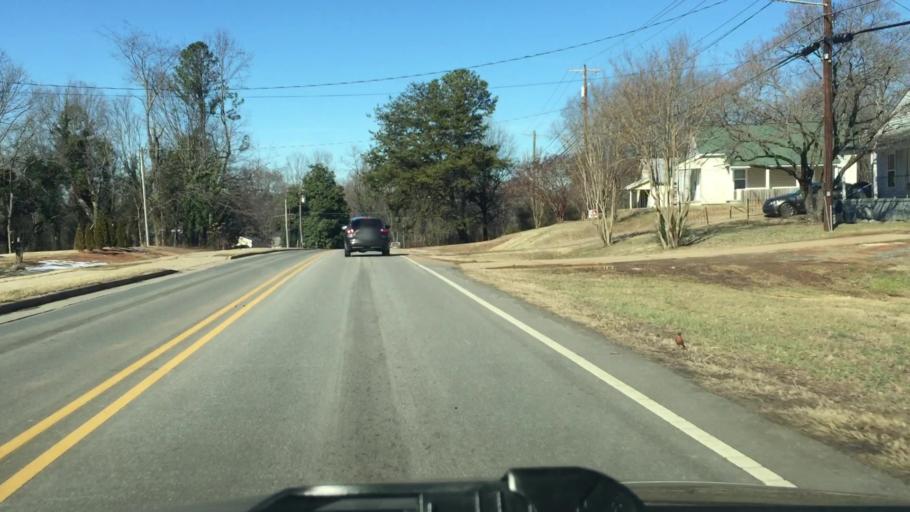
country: US
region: North Carolina
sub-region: Iredell County
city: Mooresville
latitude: 35.5901
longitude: -80.8143
